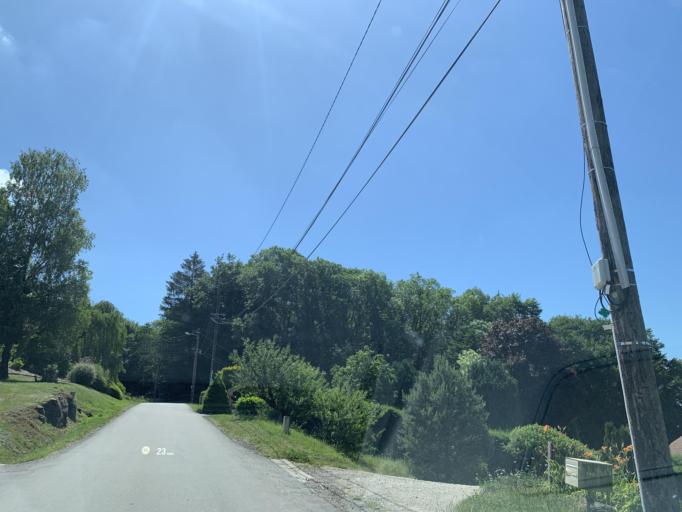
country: FR
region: Lorraine
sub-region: Departement des Vosges
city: Uzemain
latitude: 48.1376
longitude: 6.3341
